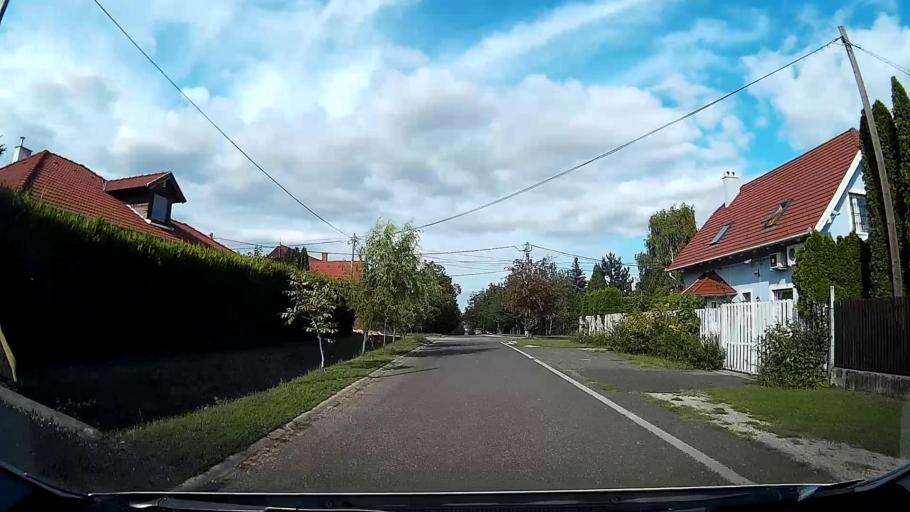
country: HU
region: Pest
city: Pomaz
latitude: 47.6333
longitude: 19.0233
